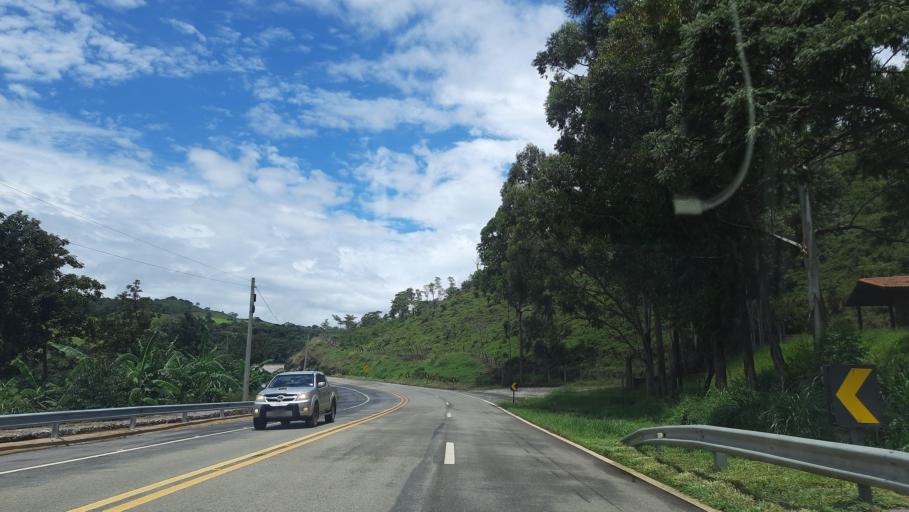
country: BR
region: Sao Paulo
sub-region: Vargem Grande Do Sul
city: Vargem Grande do Sul
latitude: -21.8324
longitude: -46.7577
